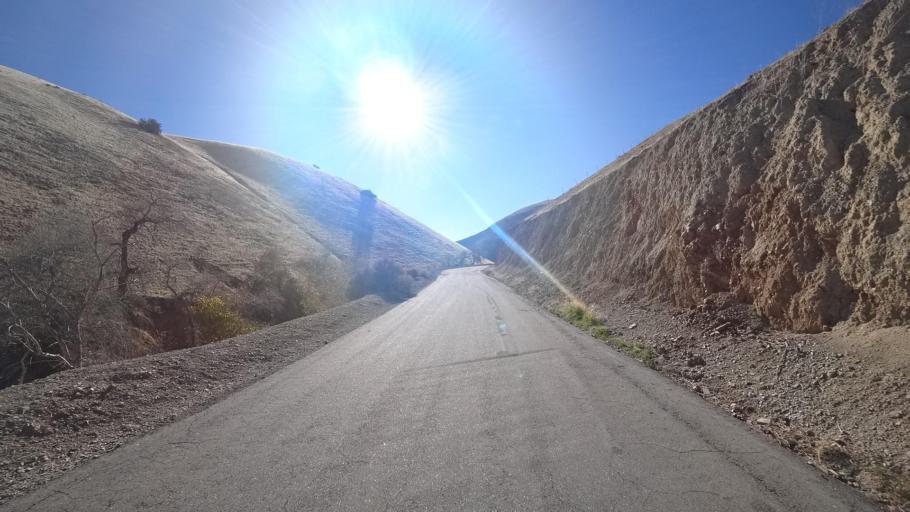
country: US
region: California
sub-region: Kern County
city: Maricopa
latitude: 34.9716
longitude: -119.4120
